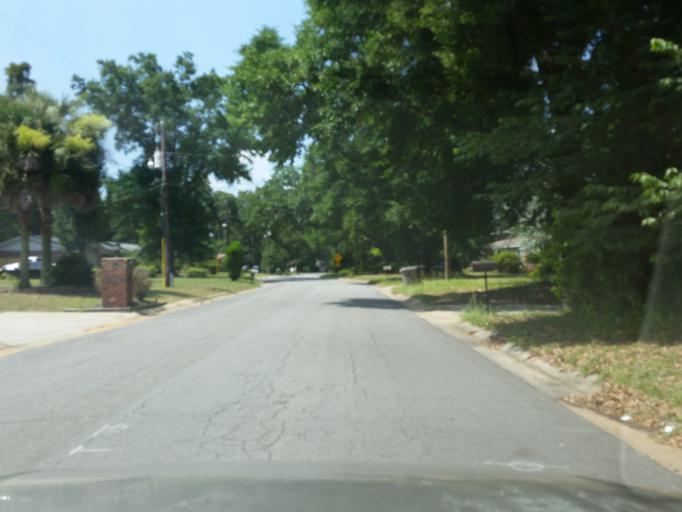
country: US
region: Florida
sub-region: Escambia County
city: Ferry Pass
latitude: 30.5103
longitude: -87.1945
